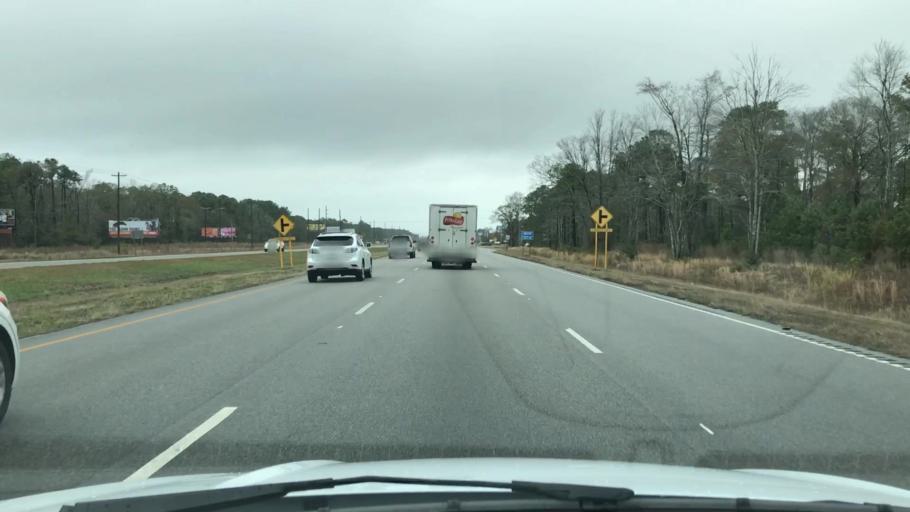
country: US
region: South Carolina
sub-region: Horry County
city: Forestbrook
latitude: 33.7693
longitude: -78.9774
